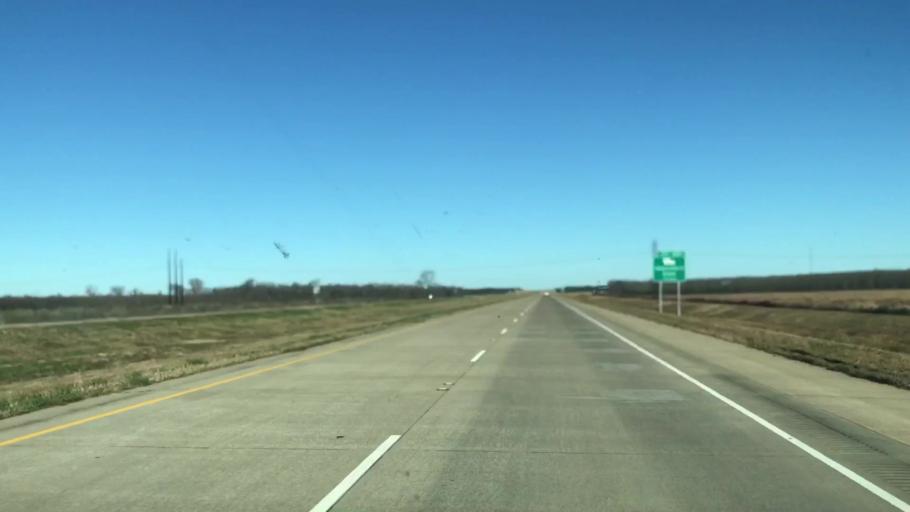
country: US
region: Louisiana
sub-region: Caddo Parish
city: Blanchard
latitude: 32.6631
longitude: -93.8452
